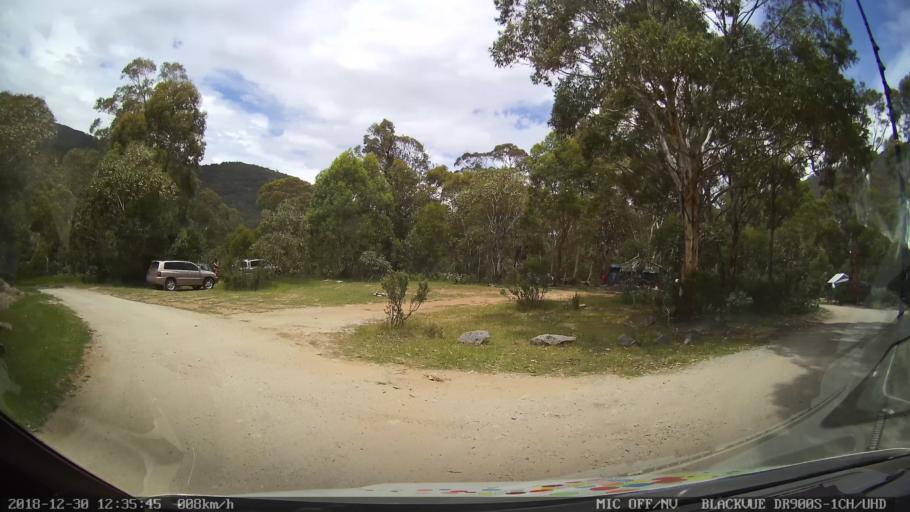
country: AU
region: New South Wales
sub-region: Snowy River
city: Jindabyne
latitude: -36.3220
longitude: 148.4643
